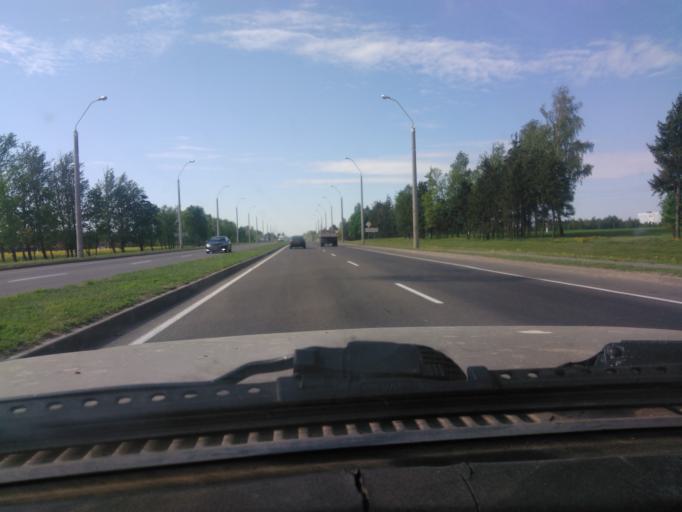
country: BY
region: Mogilev
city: Buynichy
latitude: 53.8667
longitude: 30.2604
